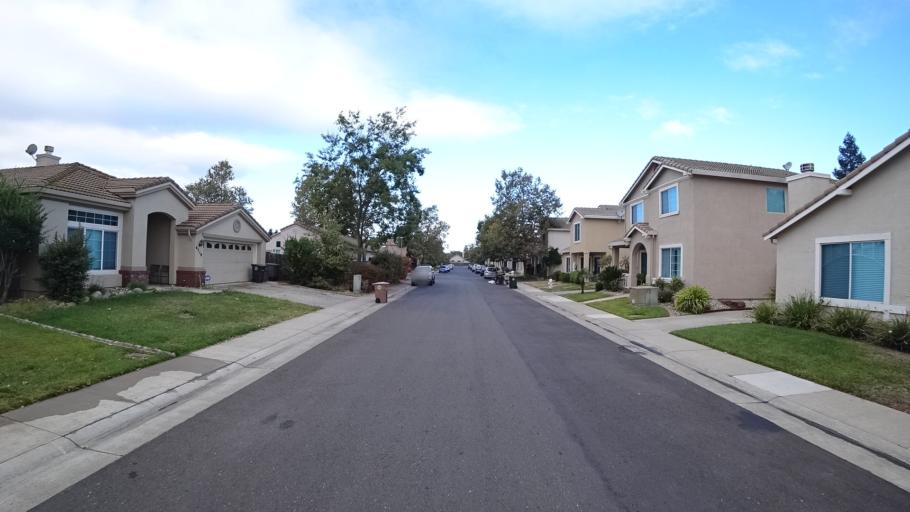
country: US
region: California
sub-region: Sacramento County
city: Laguna
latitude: 38.4331
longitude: -121.4250
